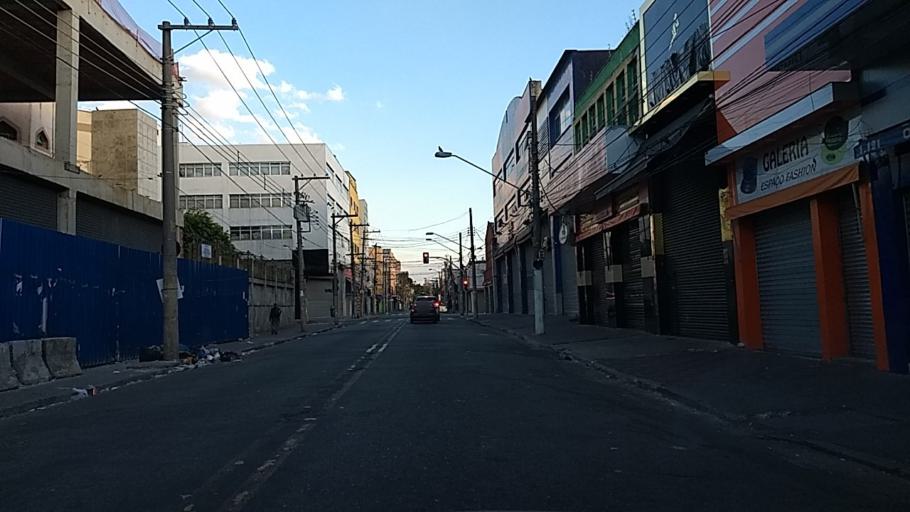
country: BR
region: Sao Paulo
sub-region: Sao Paulo
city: Sao Paulo
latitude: -23.5355
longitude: -46.6224
